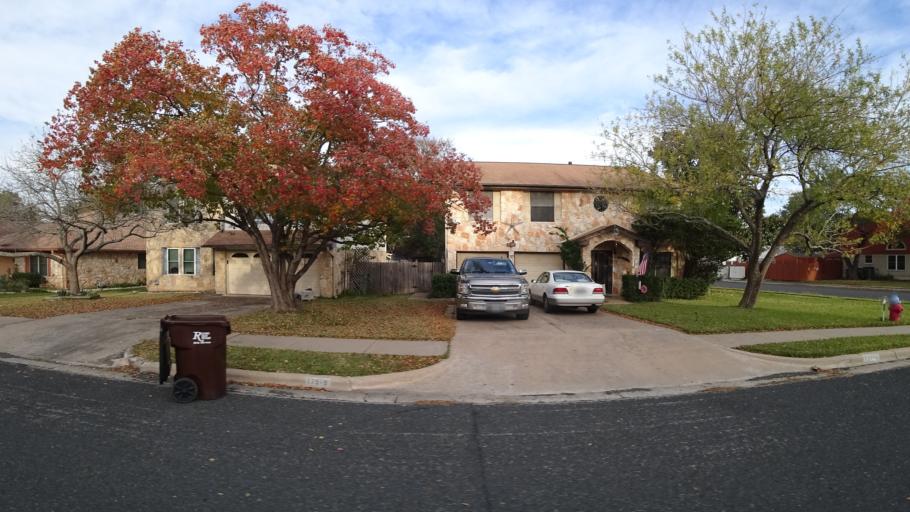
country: US
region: Texas
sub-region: Williamson County
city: Brushy Creek
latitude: 30.5134
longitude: -97.7266
